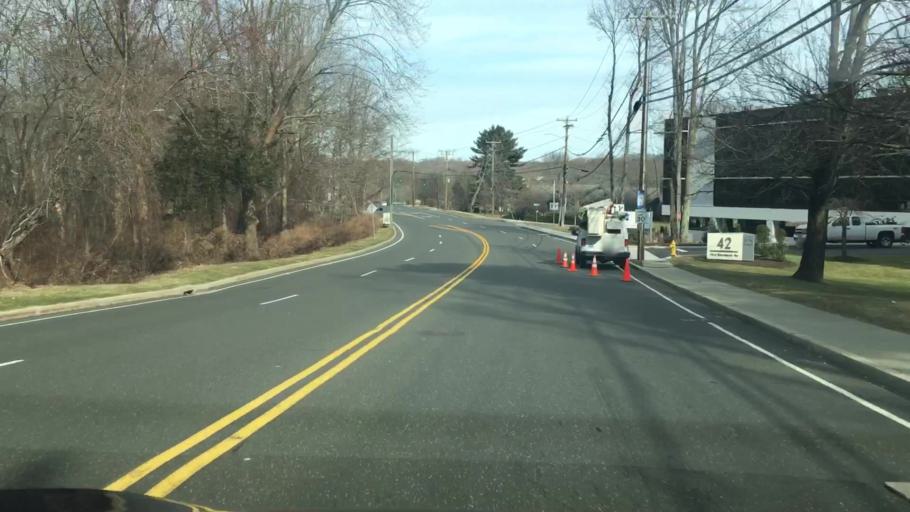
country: US
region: Connecticut
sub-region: Fairfield County
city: Danbury
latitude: 41.3838
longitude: -73.5156
